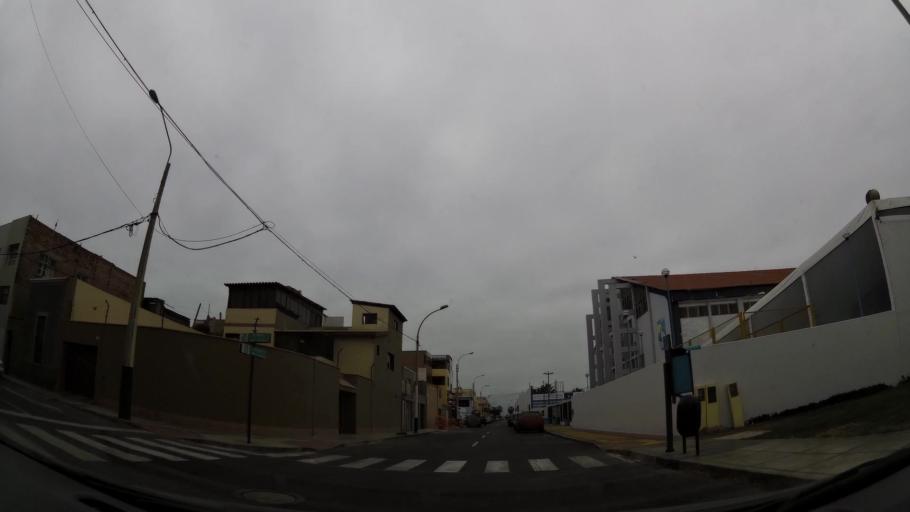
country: PE
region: Callao
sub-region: Callao
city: Callao
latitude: -12.0733
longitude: -77.1621
